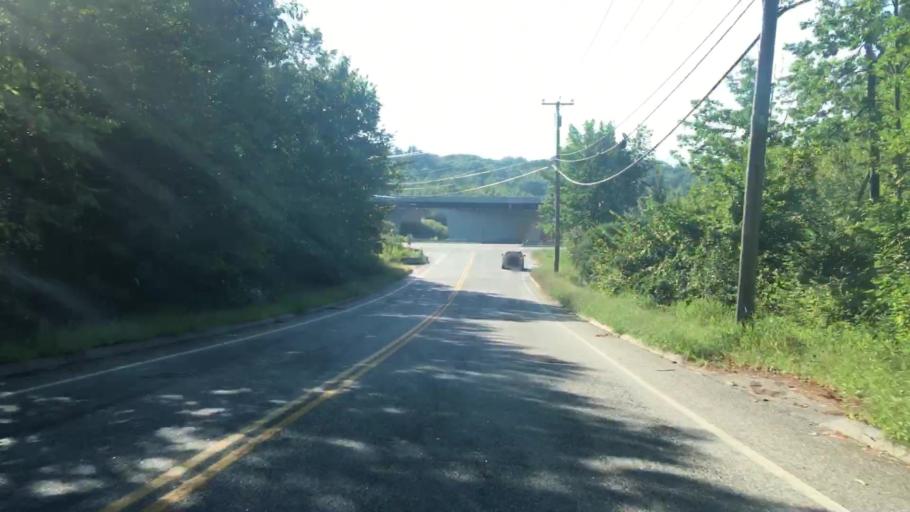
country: US
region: Maine
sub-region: Androscoggin County
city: Auburn
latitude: 44.0407
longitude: -70.2637
